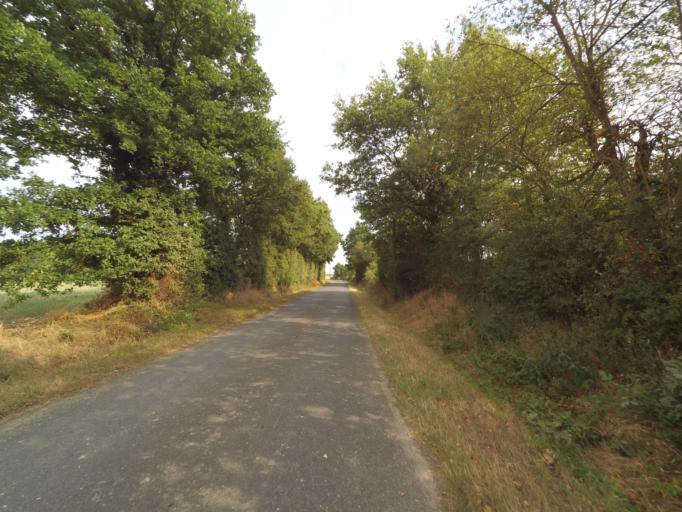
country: FR
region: Pays de la Loire
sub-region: Departement de la Vendee
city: Bouffere
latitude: 46.9829
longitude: -1.3767
